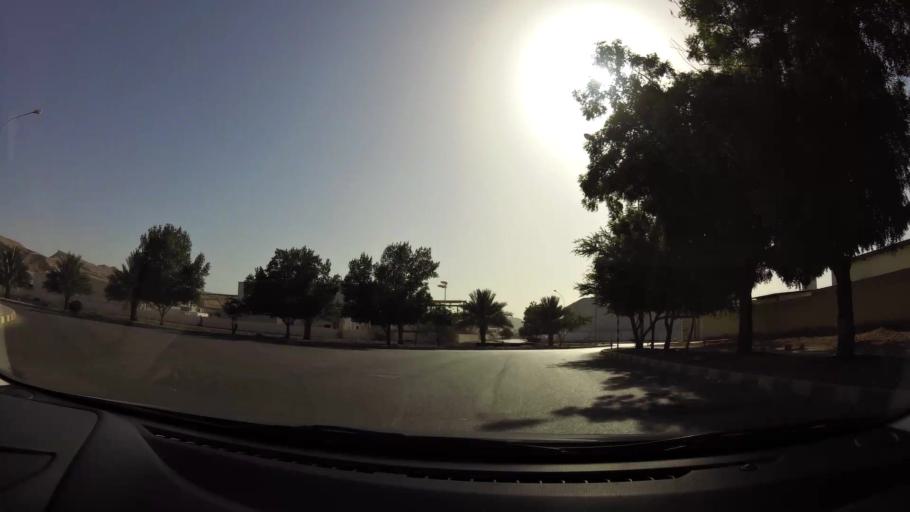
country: OM
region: Muhafazat Masqat
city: As Sib al Jadidah
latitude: 23.5550
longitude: 58.2224
